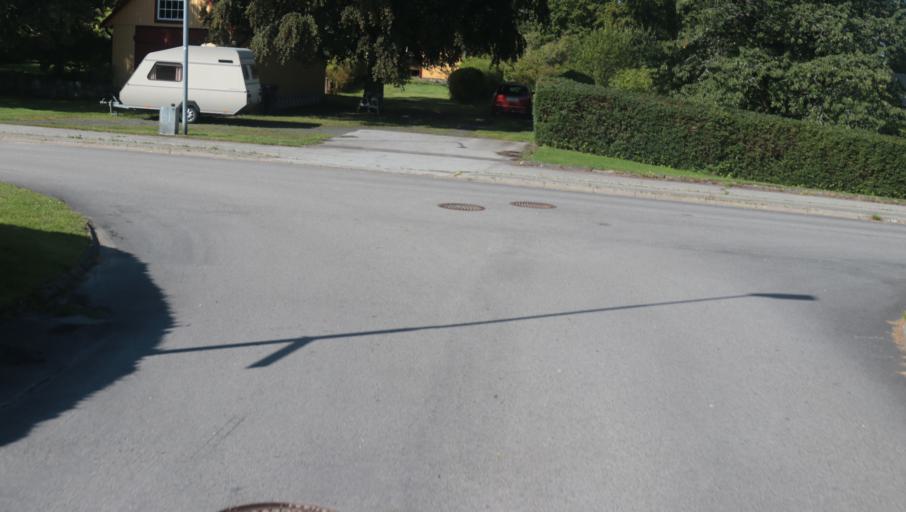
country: SE
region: Blekinge
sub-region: Karlshamns Kommun
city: Karlshamn
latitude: 56.1895
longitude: 14.8677
